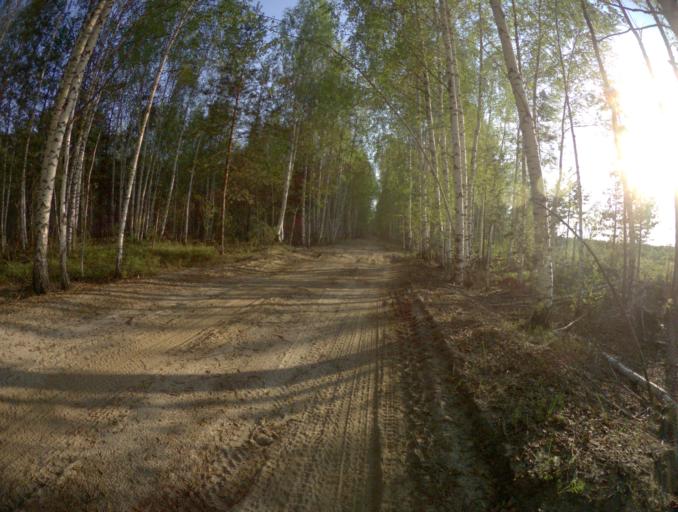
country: RU
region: Vladimir
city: Vyazniki
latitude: 56.3677
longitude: 42.1565
